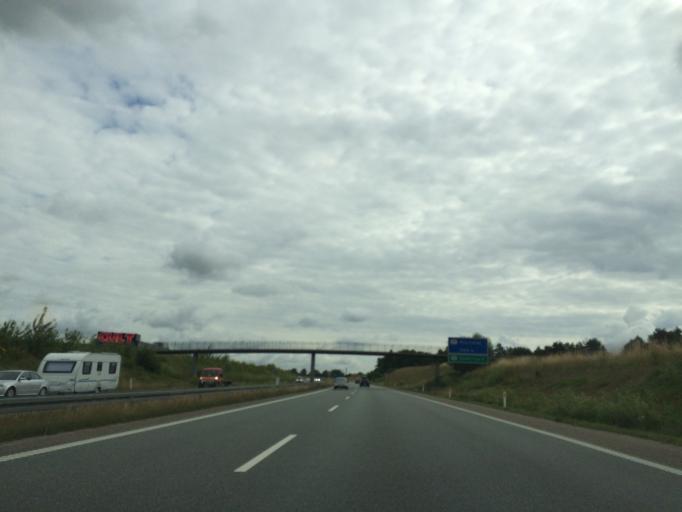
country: DK
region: Central Jutland
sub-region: Arhus Kommune
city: Lystrup
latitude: 56.2248
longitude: 10.2444
